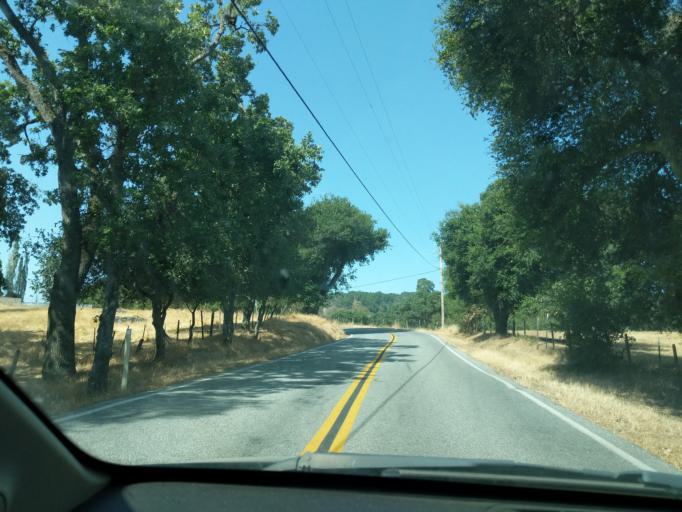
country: US
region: California
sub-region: Santa Clara County
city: Gilroy
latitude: 37.0737
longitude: -121.5171
